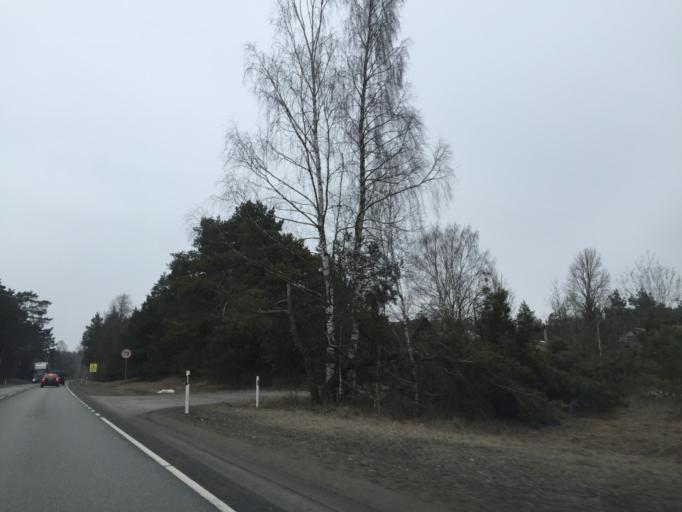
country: EE
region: Paernumaa
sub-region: Paikuse vald
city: Paikuse
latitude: 58.3181
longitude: 24.6002
